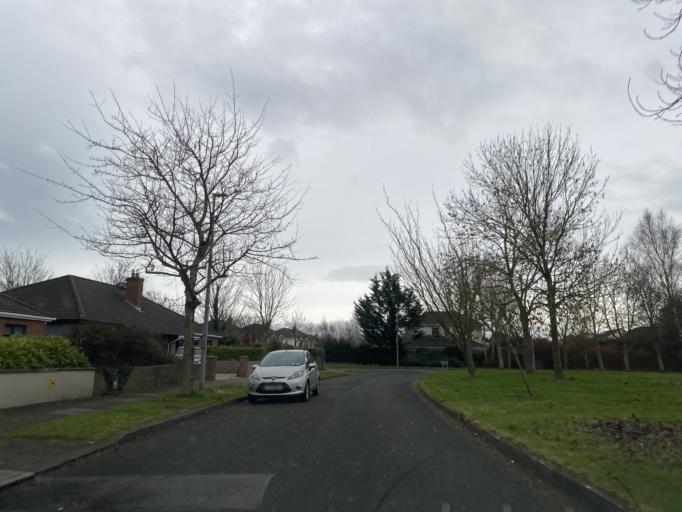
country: IE
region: Leinster
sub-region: Kildare
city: Celbridge
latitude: 53.3527
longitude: -6.5540
